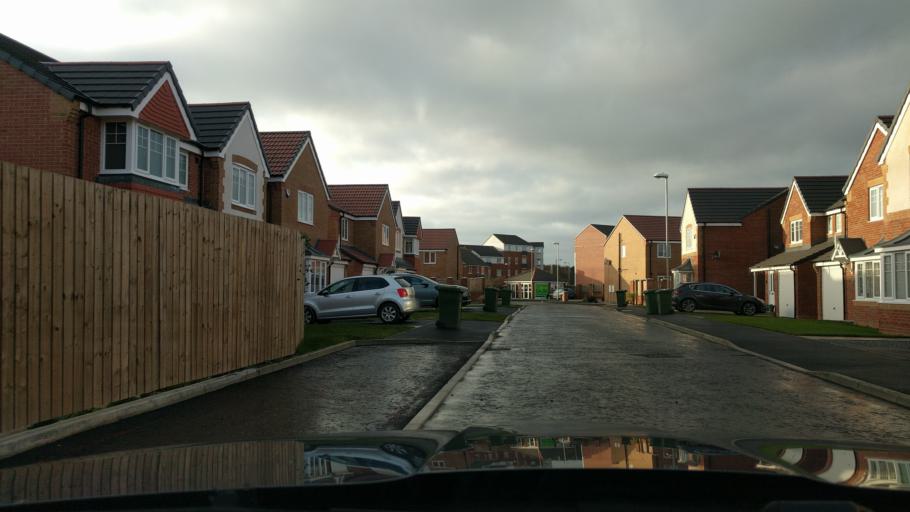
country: GB
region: England
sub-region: Northumberland
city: Ashington
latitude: 55.1881
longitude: -1.5920
